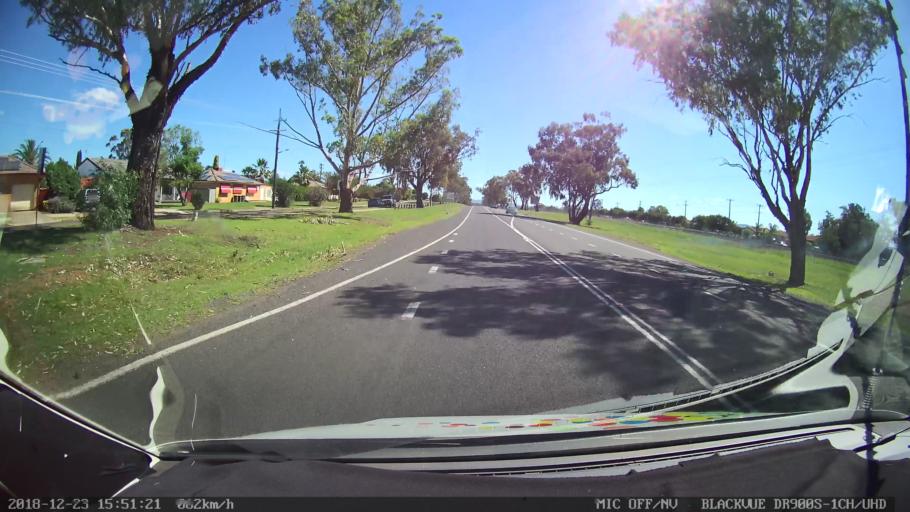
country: AU
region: New South Wales
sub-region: Tamworth Municipality
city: South Tamworth
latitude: -31.1121
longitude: 150.8964
